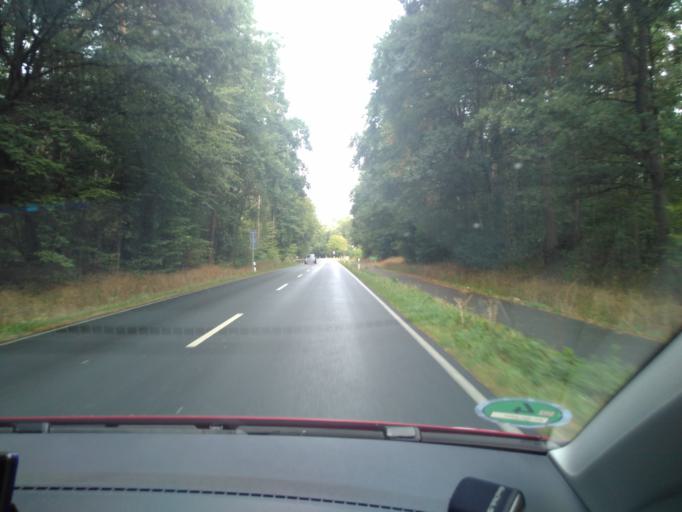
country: DE
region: North Rhine-Westphalia
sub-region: Regierungsbezirk Munster
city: Warendorf
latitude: 51.9660
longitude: 7.9754
